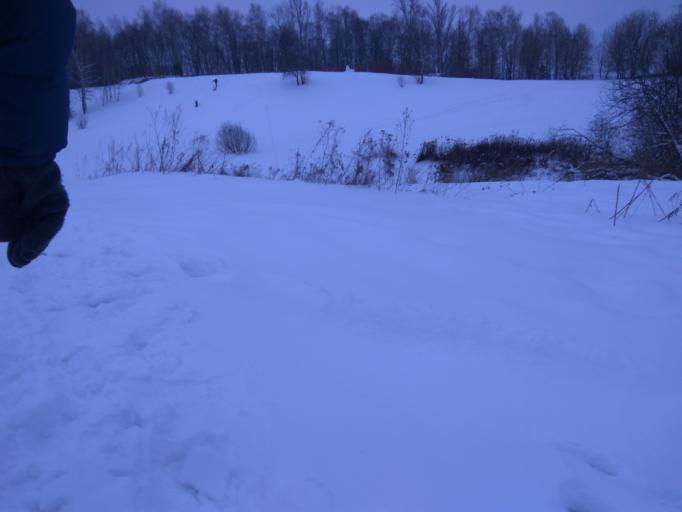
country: RU
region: Moscow
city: Orekhovo-Borisovo Severnoye
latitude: 55.6079
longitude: 37.6920
